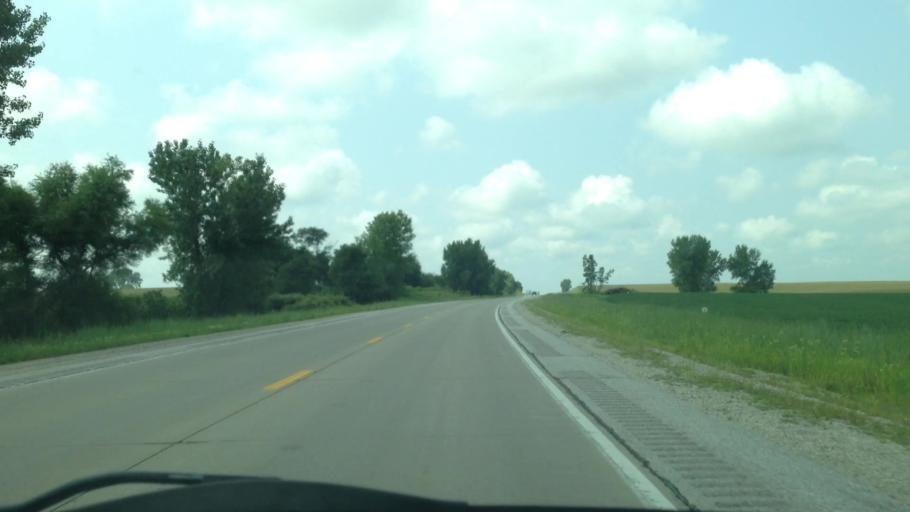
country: US
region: Iowa
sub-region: Linn County
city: Fairfax
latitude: 41.9033
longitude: -91.7996
